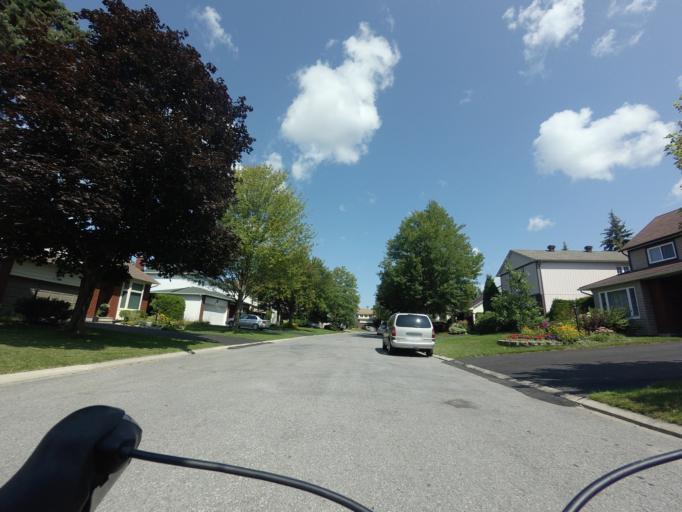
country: CA
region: Ontario
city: Bells Corners
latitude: 45.2872
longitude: -75.8660
